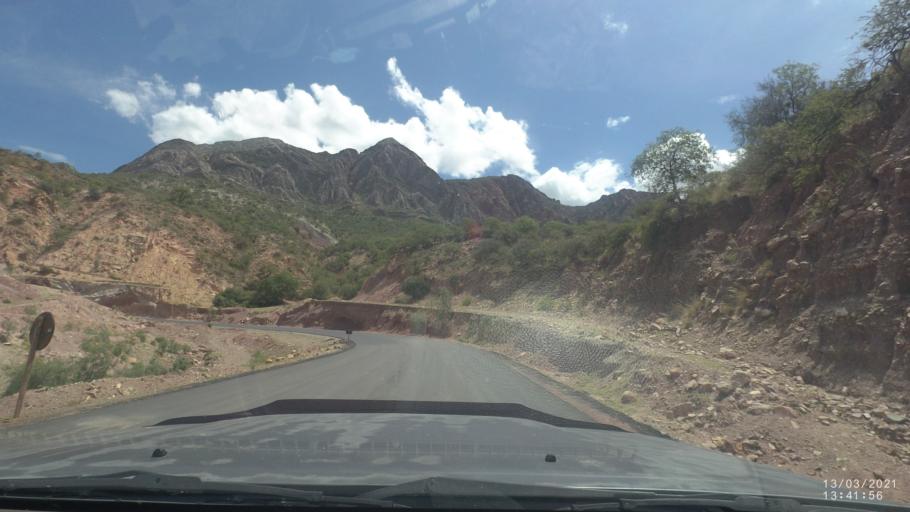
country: BO
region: Cochabamba
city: Cliza
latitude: -17.9108
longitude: -65.8796
